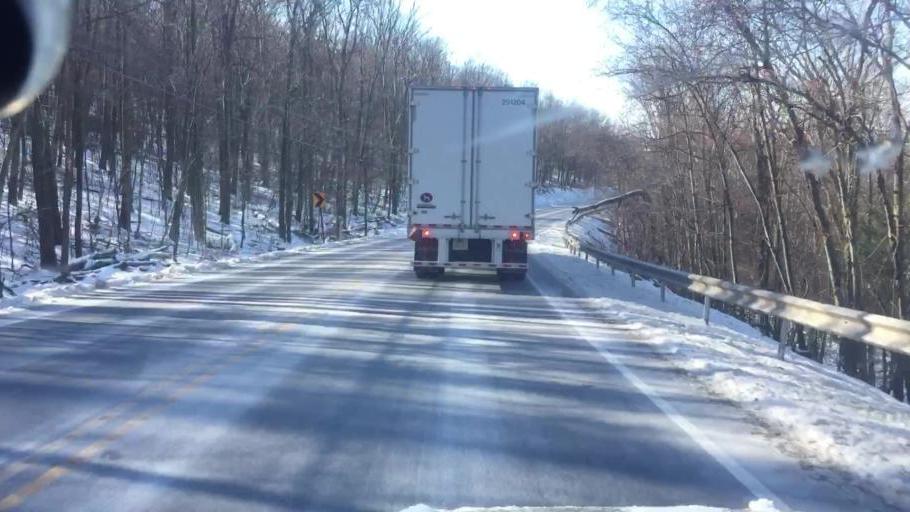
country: US
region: Pennsylvania
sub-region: Luzerne County
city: Conyngham
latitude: 41.0337
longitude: -76.1149
